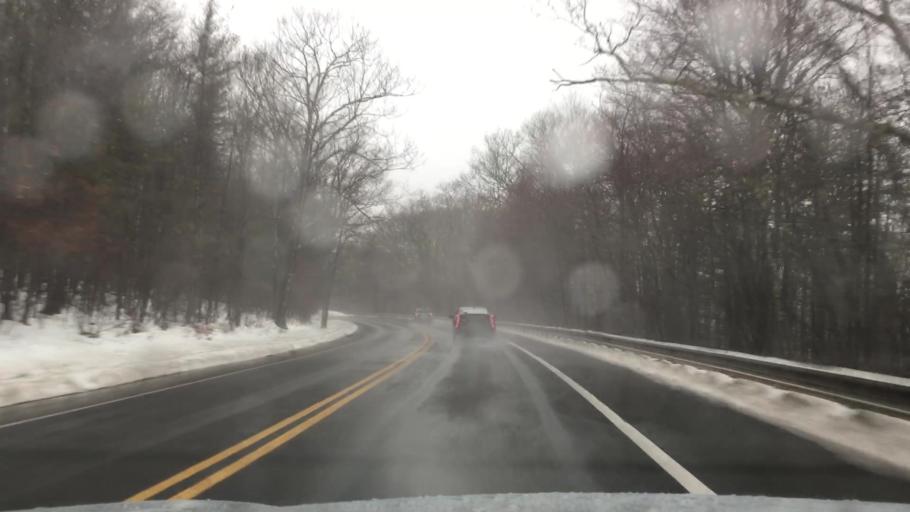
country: US
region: Massachusetts
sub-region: Franklin County
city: Shutesbury
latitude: 42.4422
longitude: -72.3876
